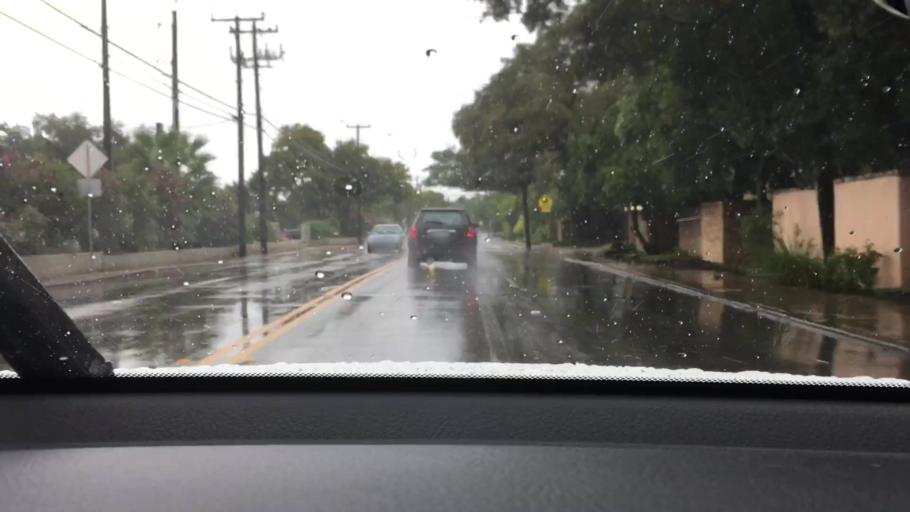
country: US
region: Texas
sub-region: Bexar County
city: Alamo Heights
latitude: 29.5047
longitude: -98.4664
